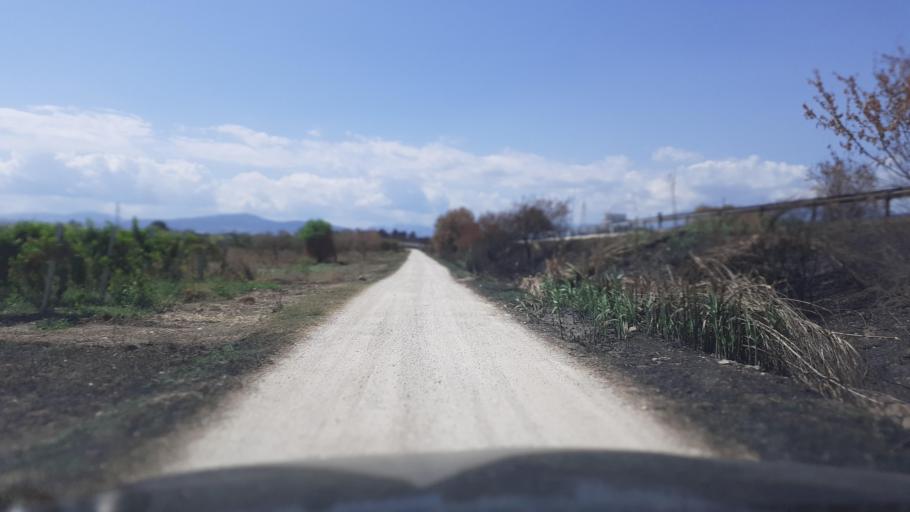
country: IT
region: Abruzzo
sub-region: Provincia di Chieti
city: Fossacesia
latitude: 42.2190
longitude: 14.4999
